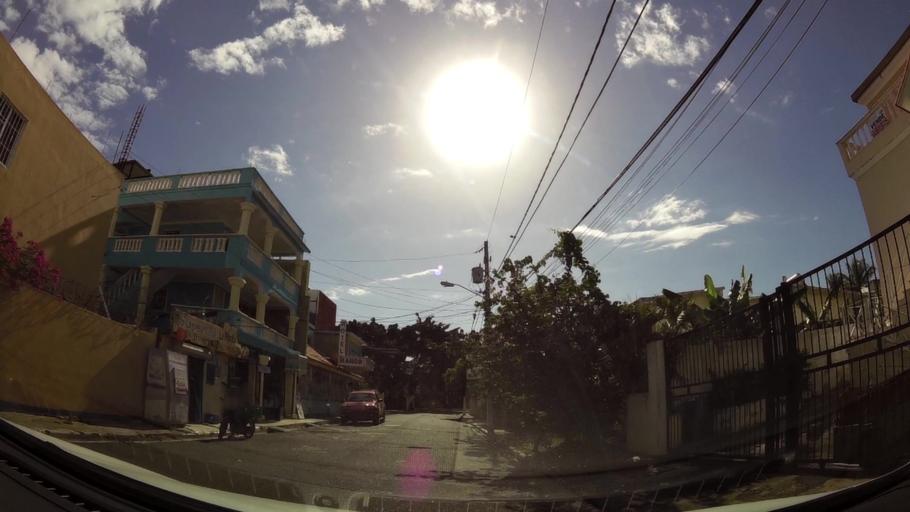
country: DO
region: Santo Domingo
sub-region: Santo Domingo
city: Boca Chica
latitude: 18.4518
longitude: -69.6082
